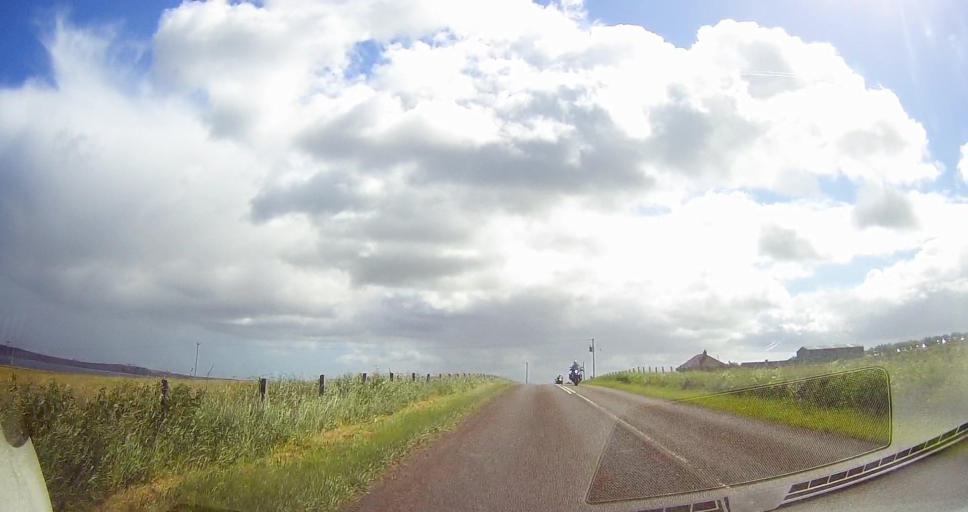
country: GB
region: Scotland
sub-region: Highland
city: Thurso
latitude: 58.5945
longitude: -3.4350
